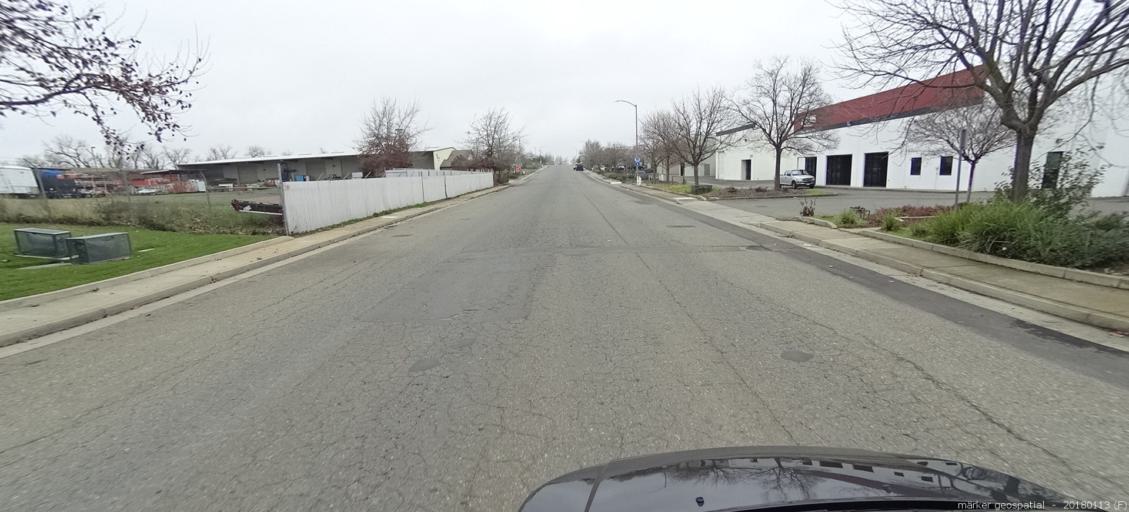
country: US
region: California
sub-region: Sacramento County
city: Gold River
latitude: 38.5830
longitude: -121.2557
